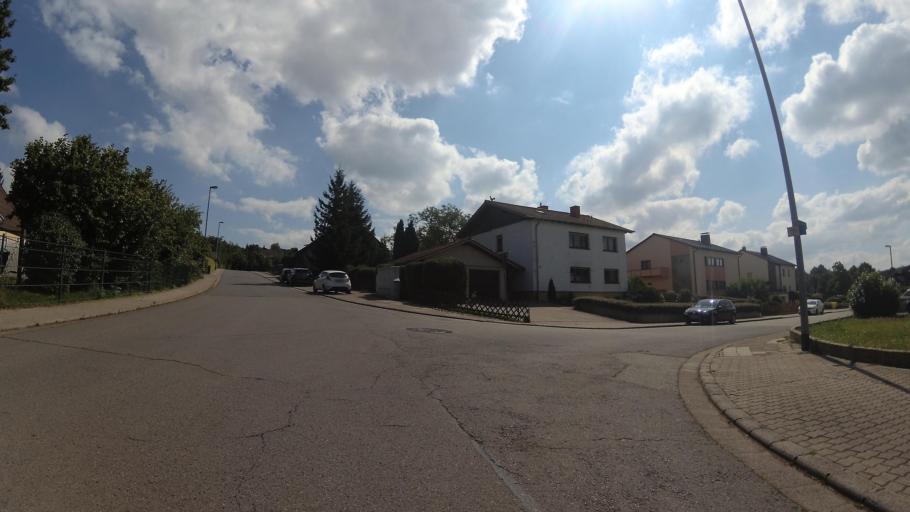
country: DE
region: Rheinland-Pfalz
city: Zweibrucken
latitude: 49.2382
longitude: 7.3696
